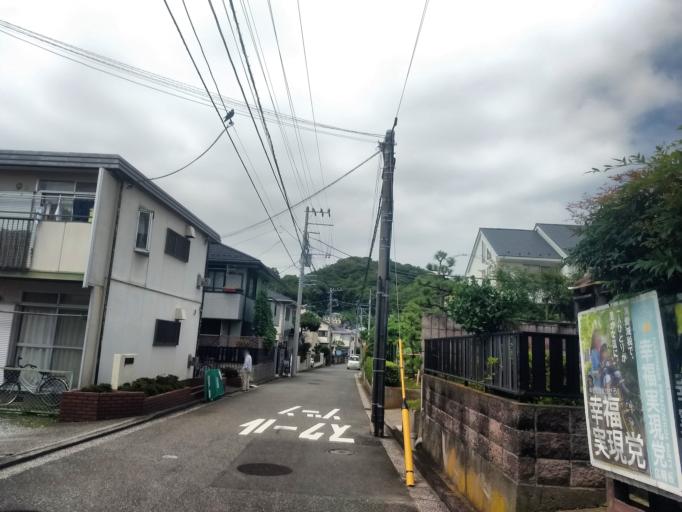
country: JP
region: Kanagawa
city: Yokosuka
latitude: 35.3419
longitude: 139.6282
